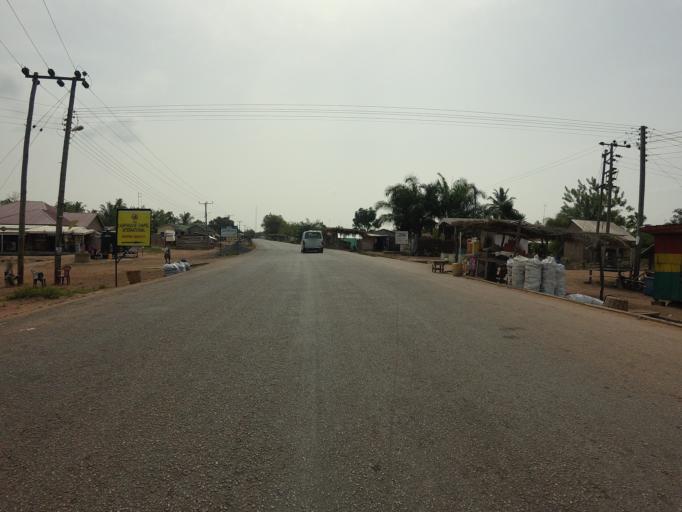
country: GH
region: Volta
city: Ho
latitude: 6.4072
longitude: 0.1735
